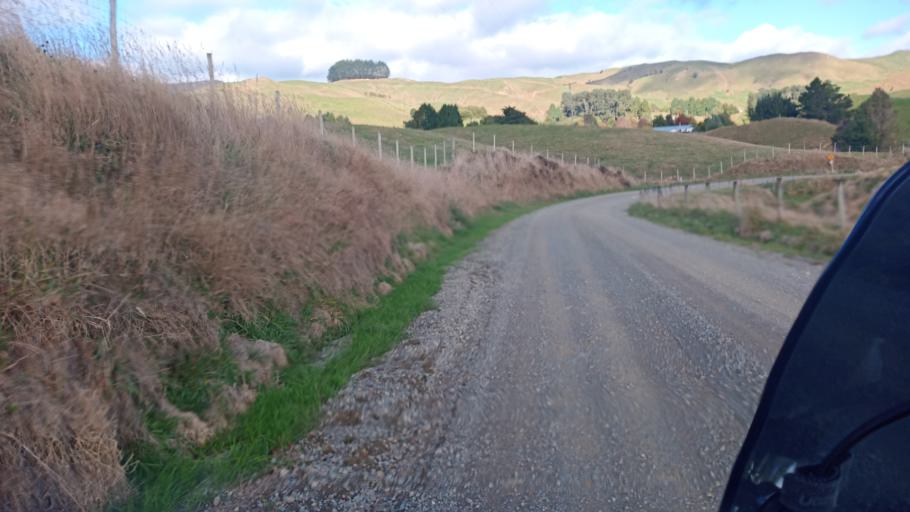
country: NZ
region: Bay of Plenty
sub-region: Opotiki District
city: Opotiki
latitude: -38.4587
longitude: 177.3895
